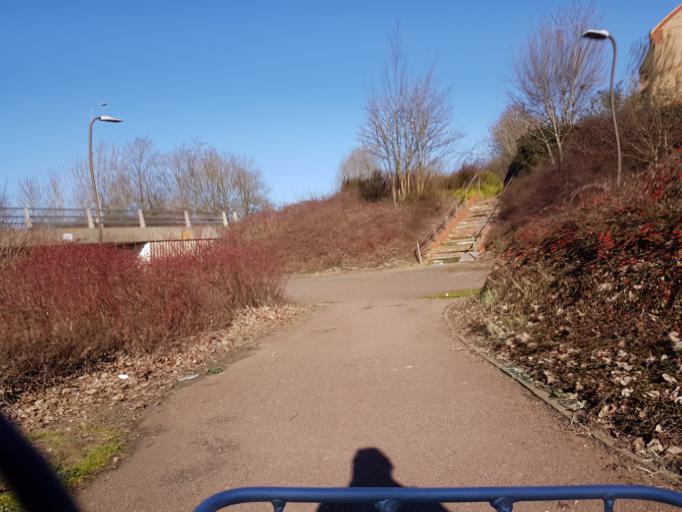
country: GB
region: England
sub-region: Milton Keynes
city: Milton Keynes
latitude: 52.0258
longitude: -0.7572
